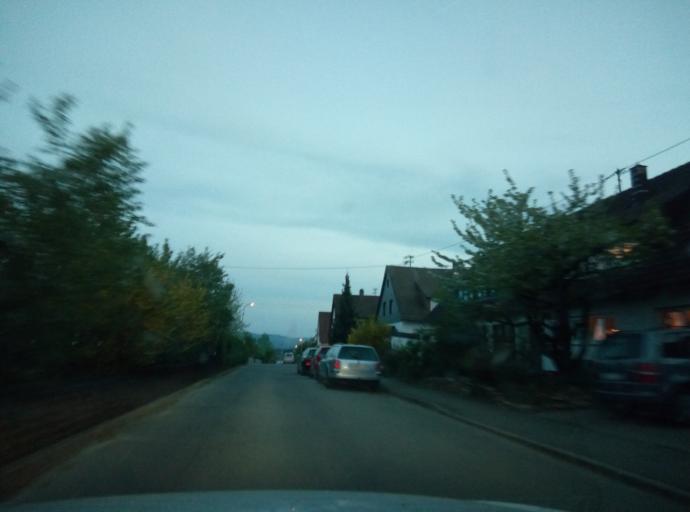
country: DE
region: Baden-Wuerttemberg
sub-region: Tuebingen Region
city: Kusterdingen
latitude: 48.5495
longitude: 9.1052
